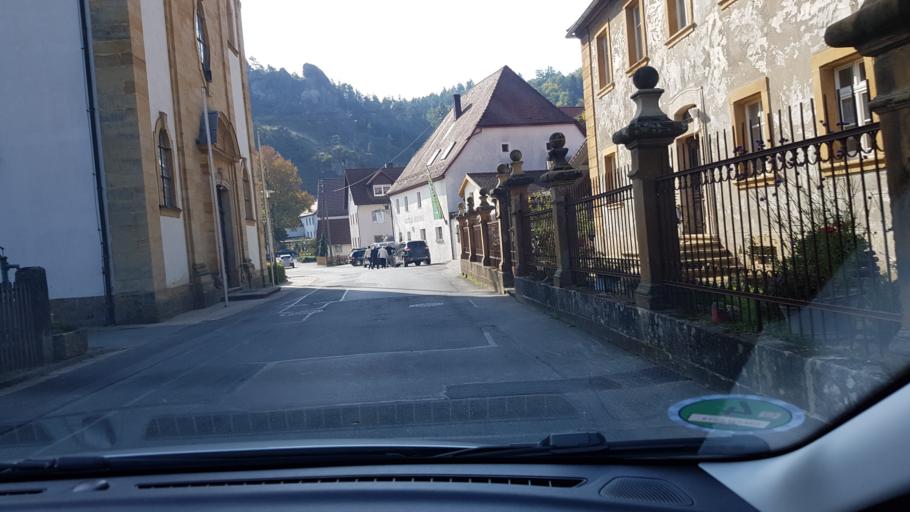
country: DE
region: Bavaria
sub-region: Upper Franconia
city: Waischenfeld
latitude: 49.8130
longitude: 11.3536
